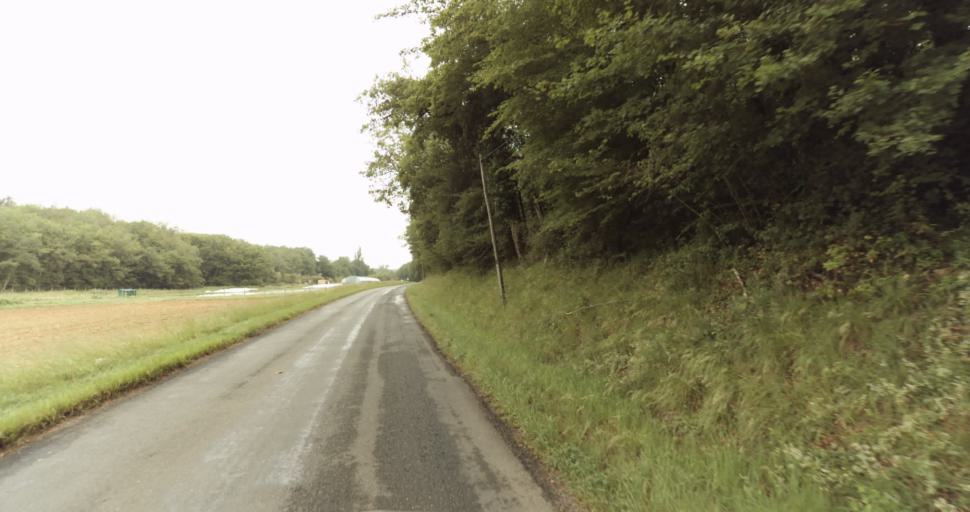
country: FR
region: Aquitaine
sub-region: Departement de la Dordogne
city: Lalinde
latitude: 44.8817
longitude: 0.7766
